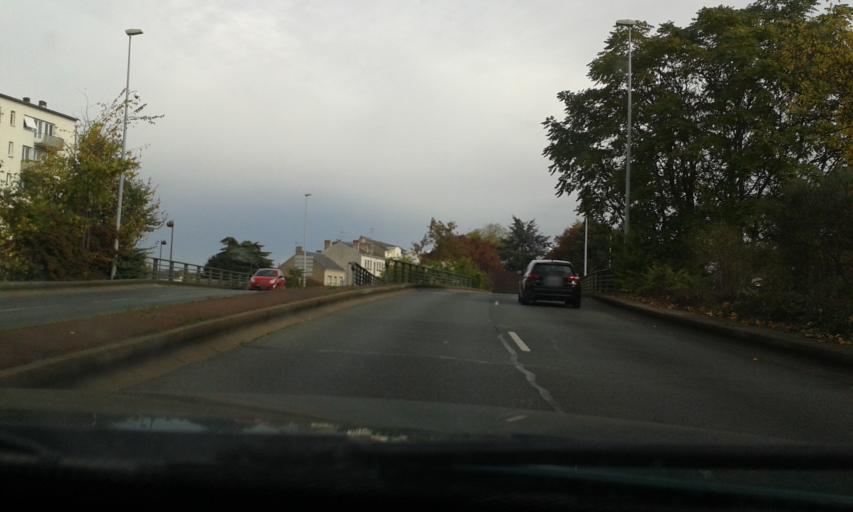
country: FR
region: Centre
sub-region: Departement du Loiret
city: Orleans
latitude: 47.9033
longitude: 1.8946
